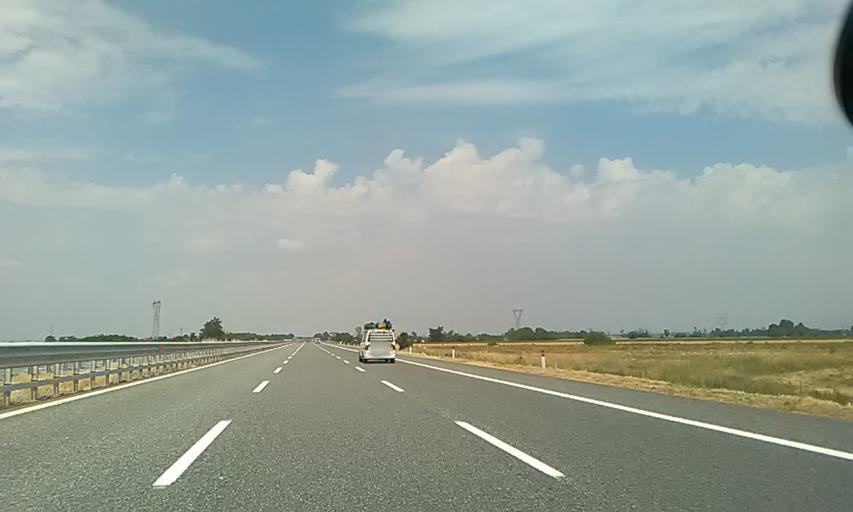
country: IT
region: Piedmont
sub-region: Provincia di Alessandria
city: Castelspina
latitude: 44.7926
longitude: 8.6127
